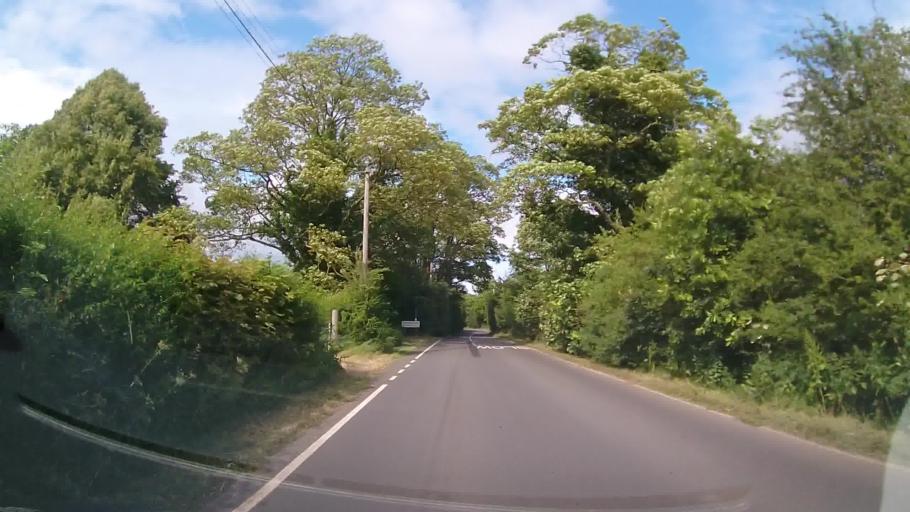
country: GB
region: England
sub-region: Shropshire
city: Petton
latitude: 52.8556
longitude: -2.7919
